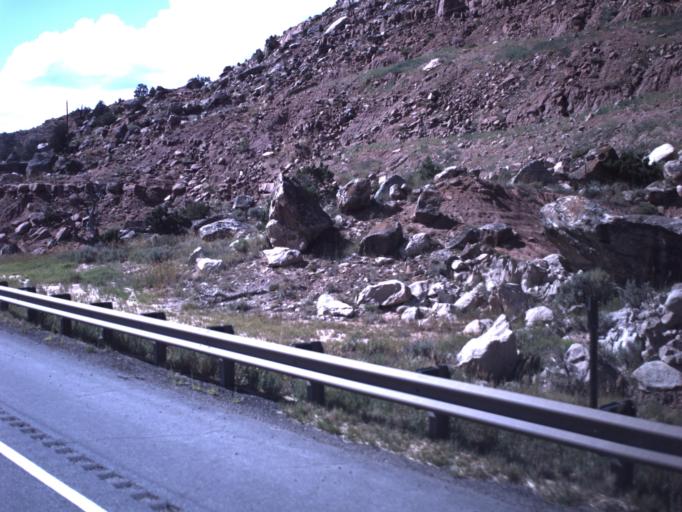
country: US
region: Utah
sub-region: Duchesne County
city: Duchesne
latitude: 40.1987
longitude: -110.8989
